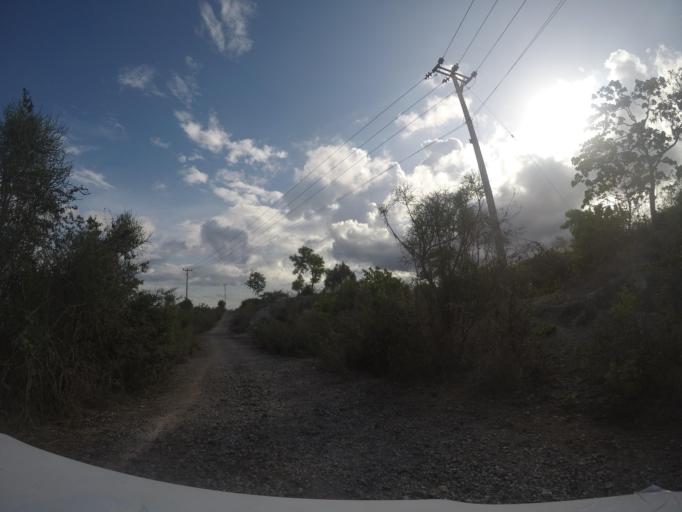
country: TL
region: Baucau
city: Baucau
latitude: -8.4712
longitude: 126.4648
